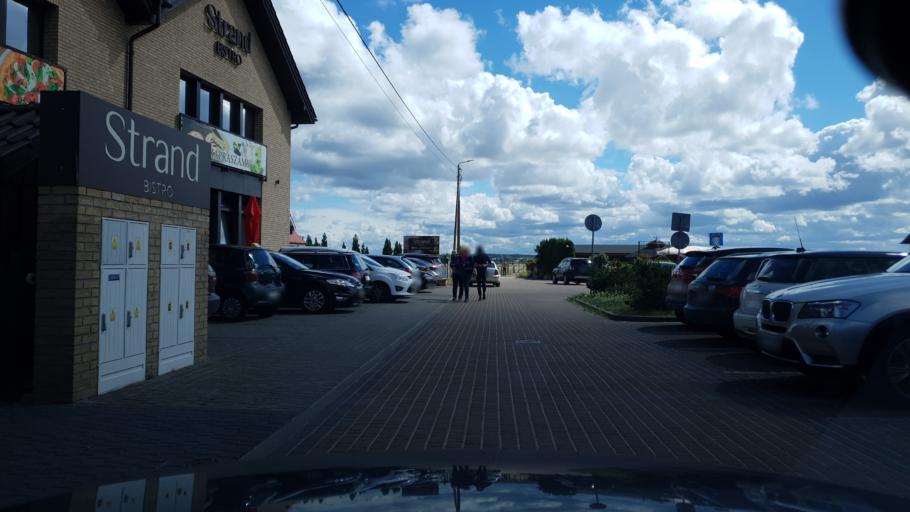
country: PL
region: Pomeranian Voivodeship
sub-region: Powiat pucki
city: Mosty
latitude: 54.6318
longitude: 18.5122
